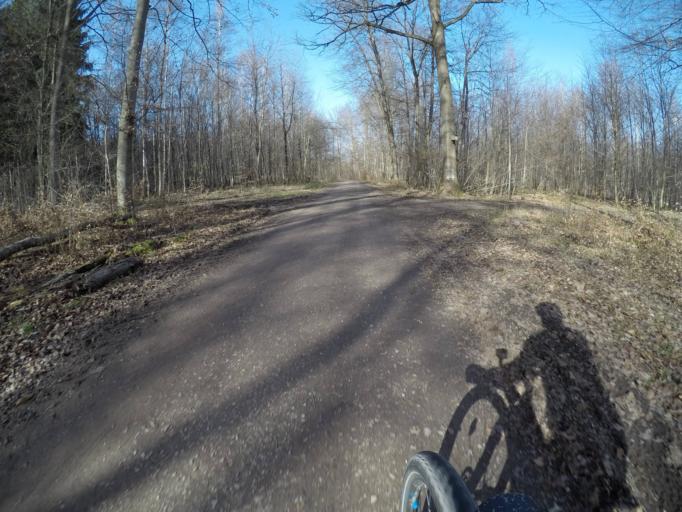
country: DE
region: Baden-Wuerttemberg
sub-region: Regierungsbezirk Stuttgart
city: Hochdorf
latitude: 48.6802
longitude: 9.4668
